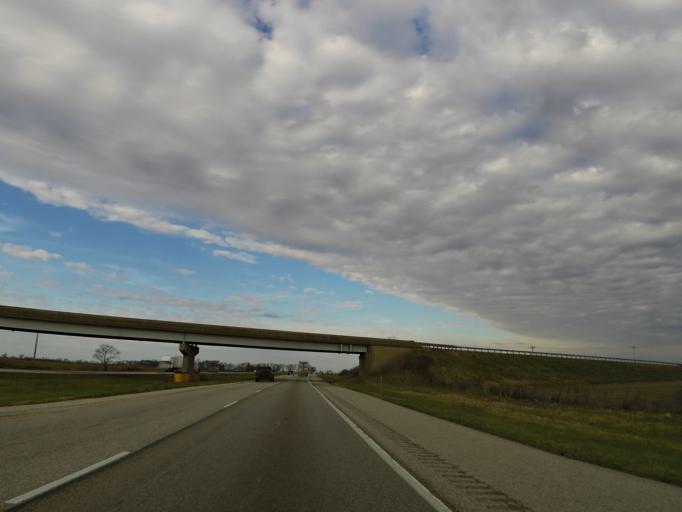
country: US
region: Illinois
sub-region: Washington County
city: Nashville
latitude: 38.4134
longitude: -89.4352
